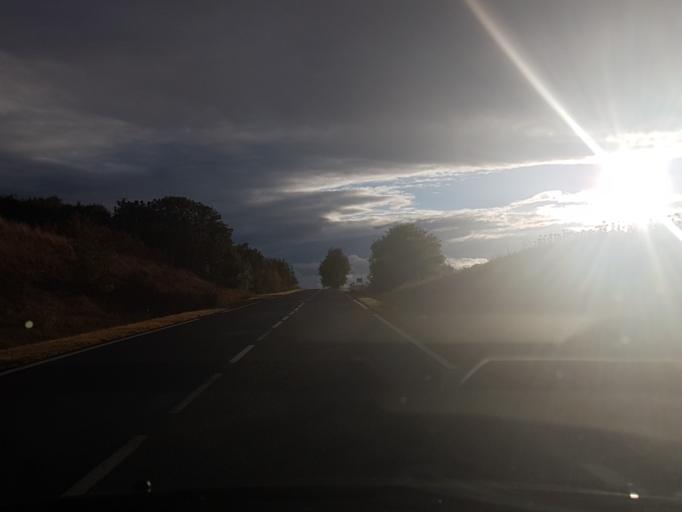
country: FR
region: Languedoc-Roussillon
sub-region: Departement de l'Aude
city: Bram
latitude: 43.1741
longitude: 2.0097
